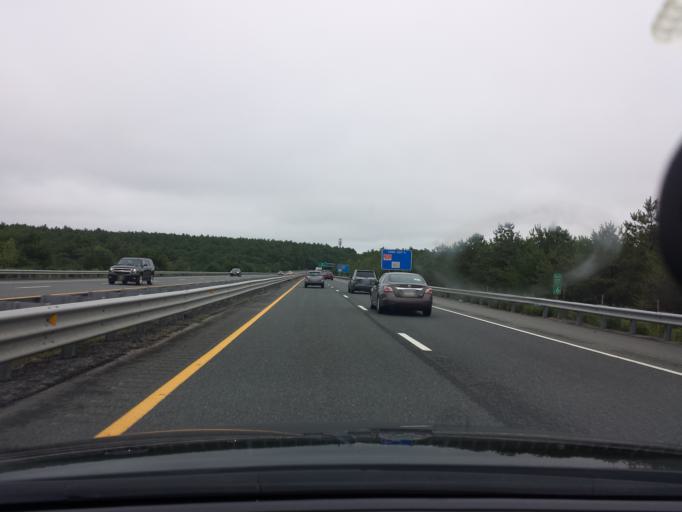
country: US
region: Rhode Island
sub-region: Kent County
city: West Greenwich
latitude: 41.6462
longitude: -71.6173
